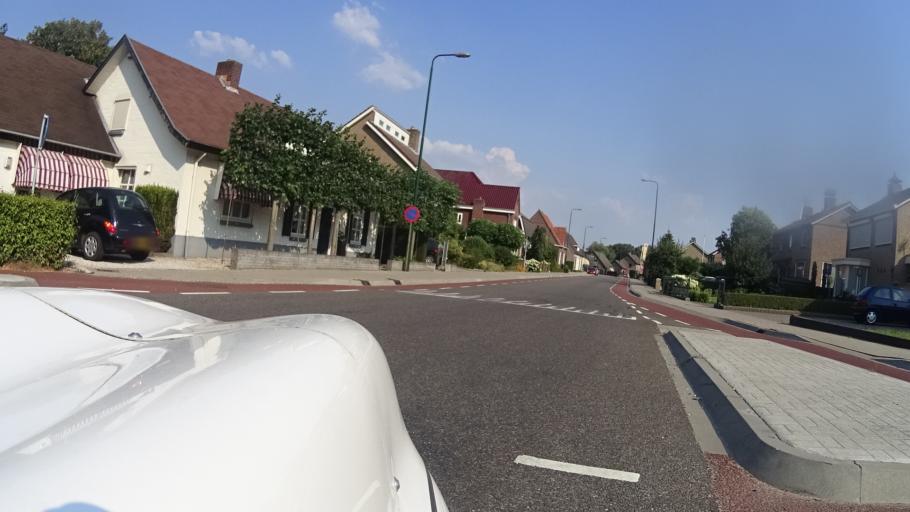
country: NL
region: North Brabant
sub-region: Gemeente Mill en Sint Hubert
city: Wilbertoord
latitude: 51.6922
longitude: 5.7813
